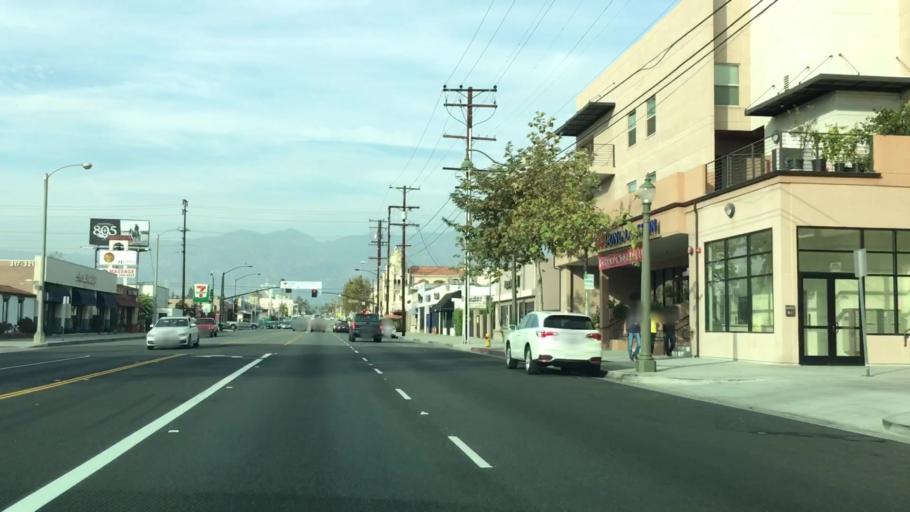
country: US
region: California
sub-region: Los Angeles County
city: East San Gabriel
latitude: 34.0975
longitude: -118.0909
